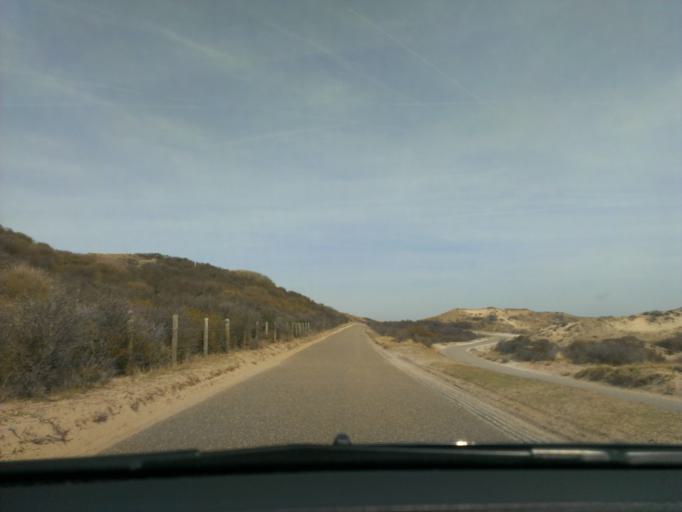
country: NL
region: North Holland
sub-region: Gemeente Zandvoort
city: Zandvoort
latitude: 52.4091
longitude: 4.5496
